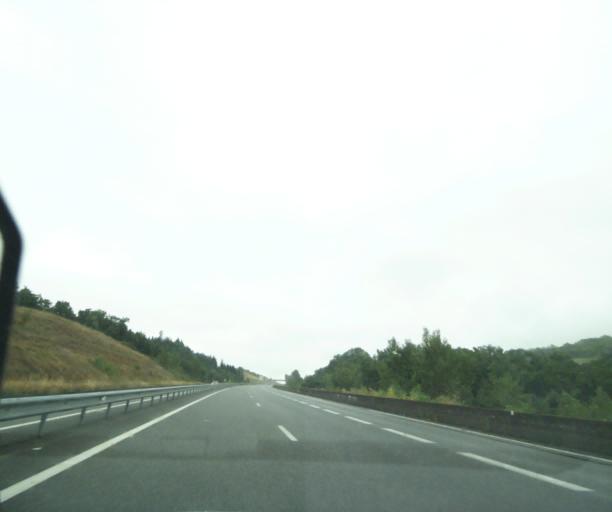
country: FR
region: Midi-Pyrenees
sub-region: Departement du Tarn
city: Le Garric
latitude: 44.0044
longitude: 2.1732
